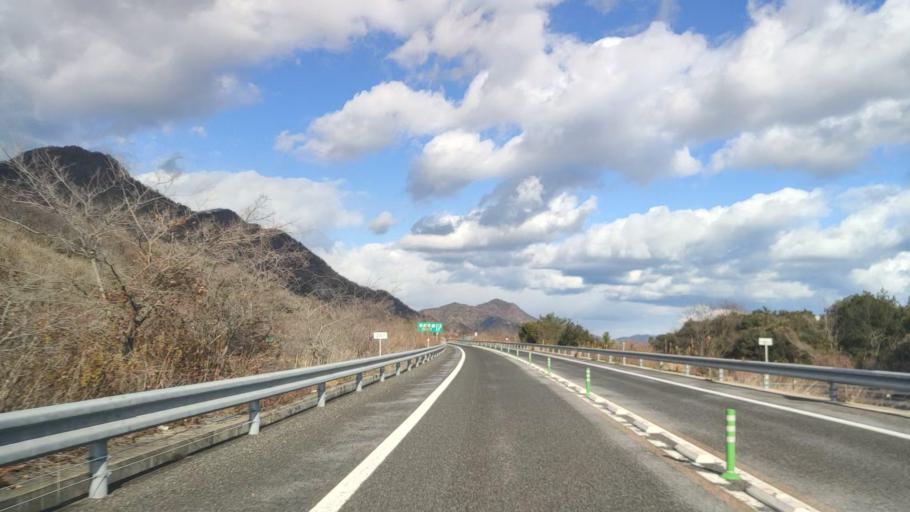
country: JP
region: Hiroshima
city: Innoshima
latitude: 34.2629
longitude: 133.0932
